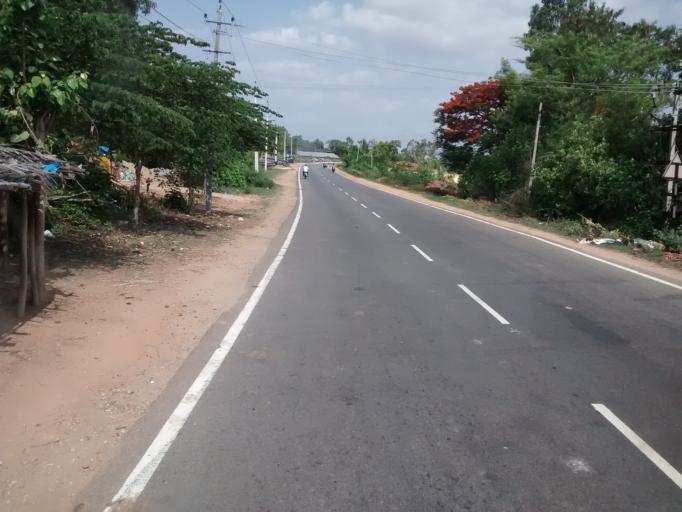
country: IN
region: Karnataka
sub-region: Mysore
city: Hunsur
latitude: 12.3631
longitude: 76.4206
